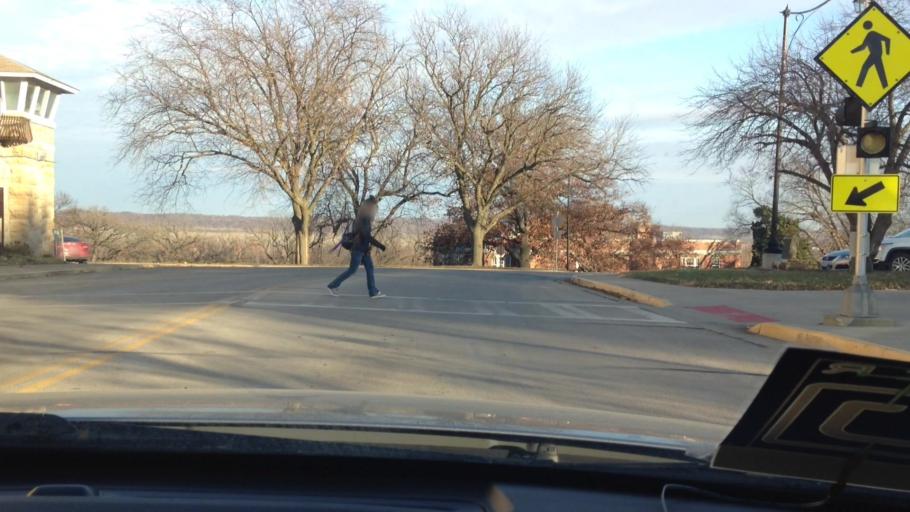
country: US
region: Kansas
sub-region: Leavenworth County
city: Leavenworth
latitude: 39.3578
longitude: -94.9170
